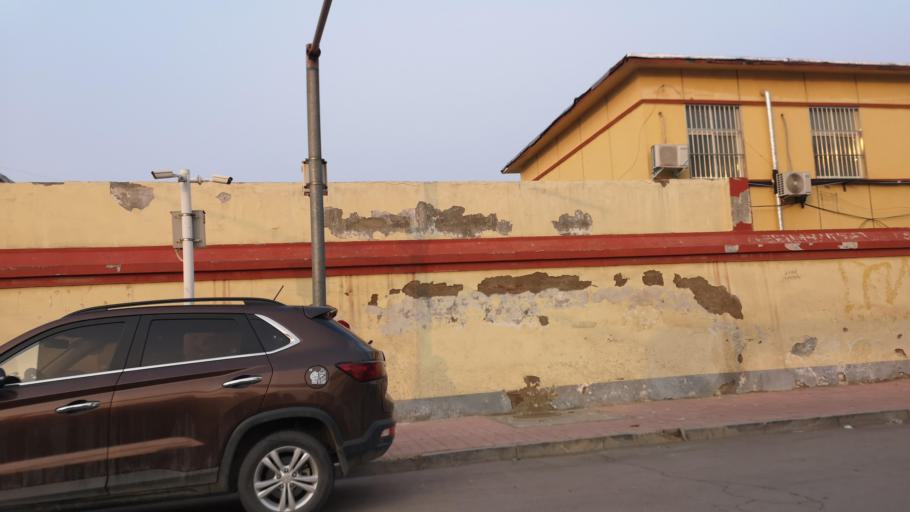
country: CN
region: Henan Sheng
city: Zhongyuanlu
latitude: 35.7687
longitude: 115.1009
